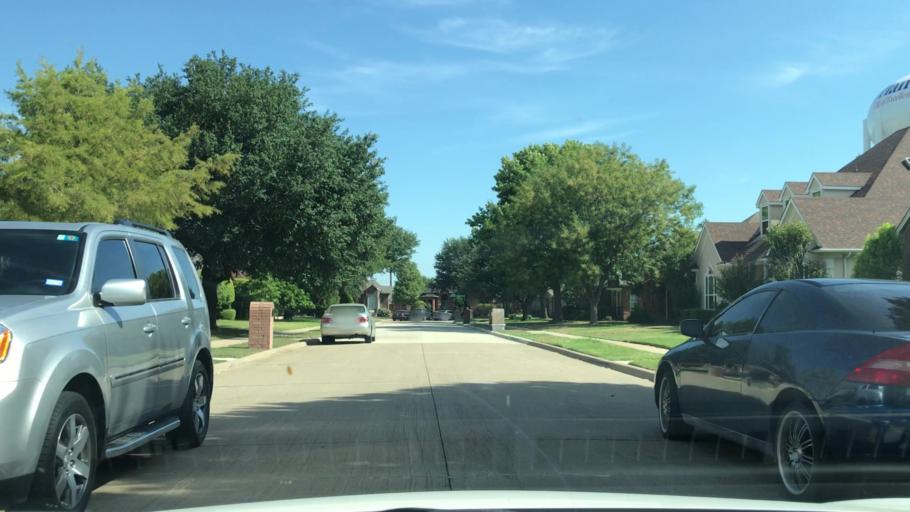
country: US
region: Texas
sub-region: Collin County
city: Plano
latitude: 33.0547
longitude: -96.7650
